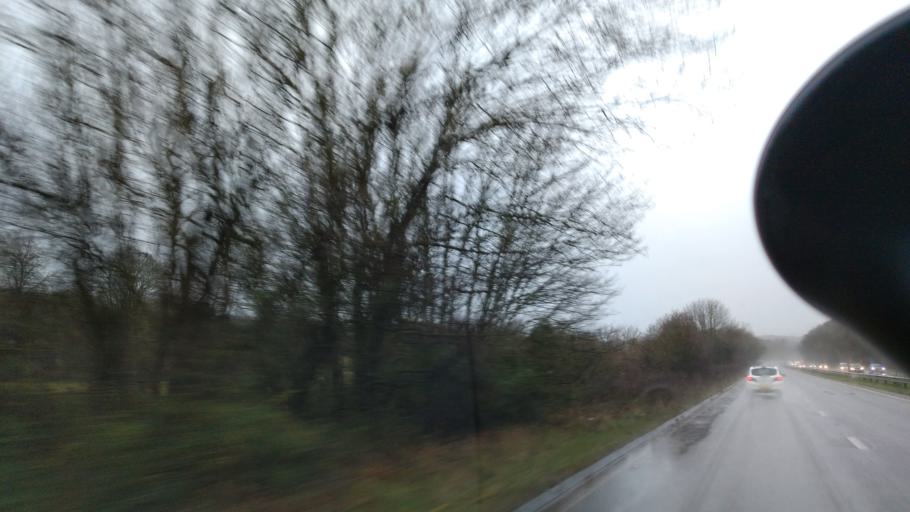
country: GB
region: England
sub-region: East Sussex
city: Lewes
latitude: 50.8659
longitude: -0.0335
